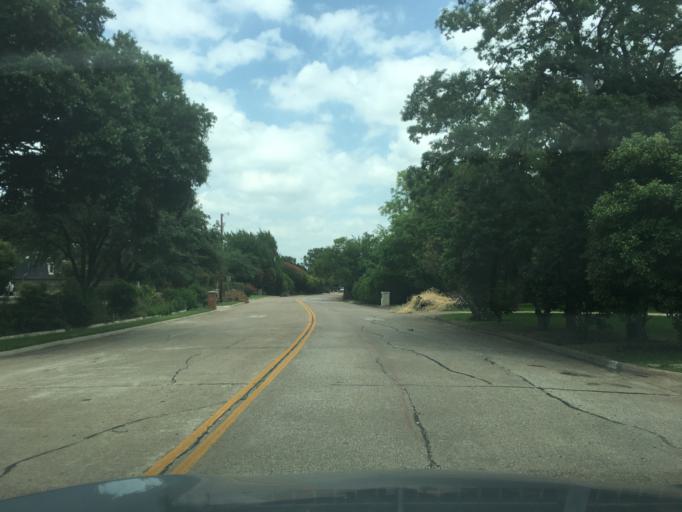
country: US
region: Texas
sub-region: Dallas County
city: University Park
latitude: 32.9021
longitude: -96.8279
